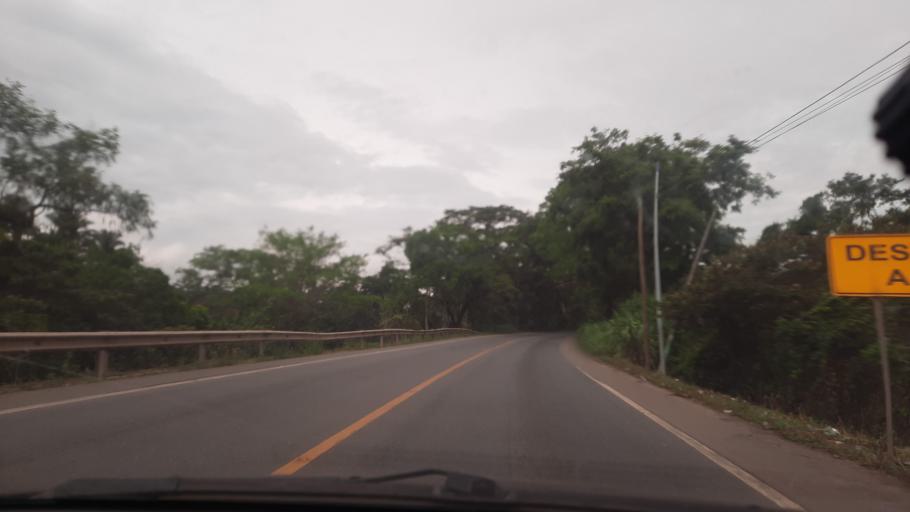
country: GT
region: Izabal
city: Morales
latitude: 15.5075
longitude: -88.8085
